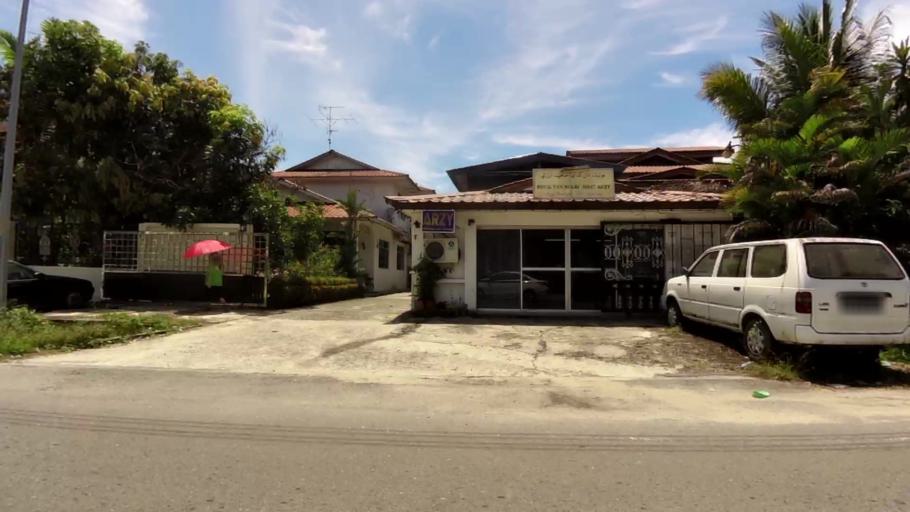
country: BN
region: Brunei and Muara
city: Bandar Seri Begawan
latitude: 4.9439
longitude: 114.9489
